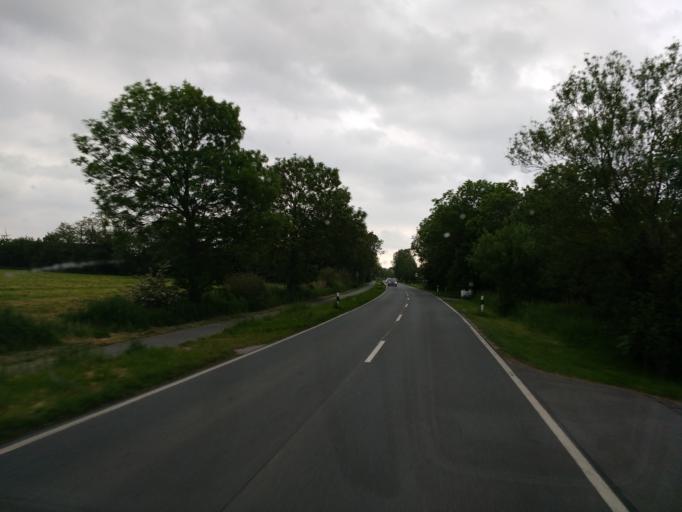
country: DE
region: Lower Saxony
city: Schillig
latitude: 53.6542
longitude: 7.9912
